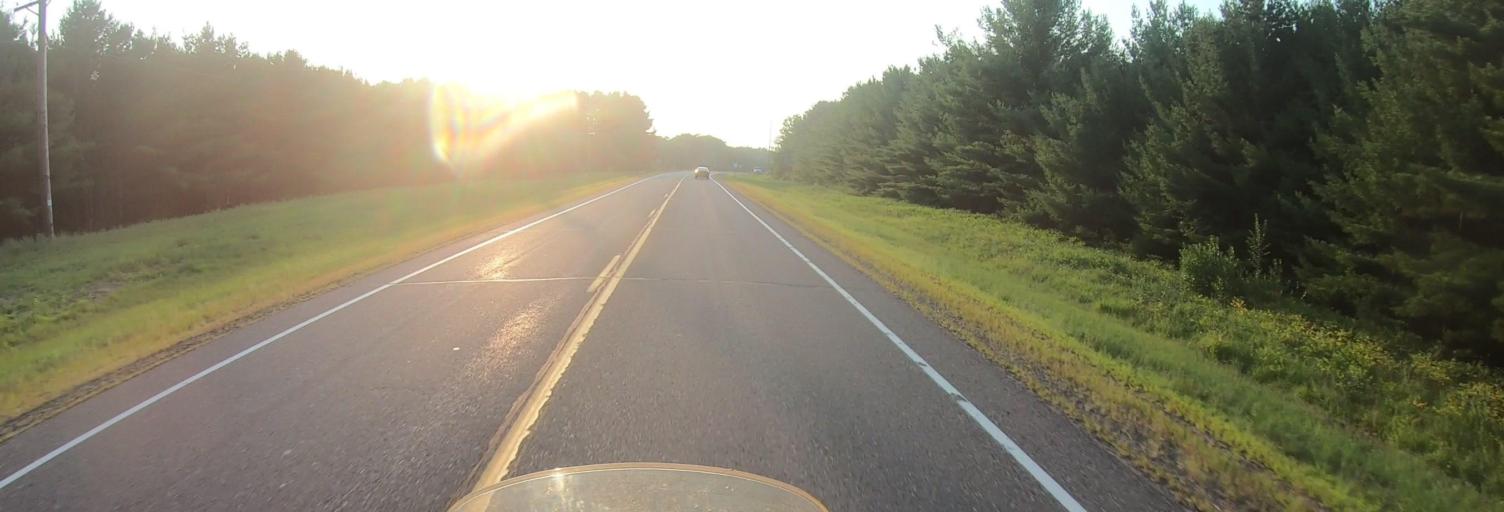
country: US
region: Wisconsin
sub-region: Burnett County
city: Siren
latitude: 45.8145
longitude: -92.2343
